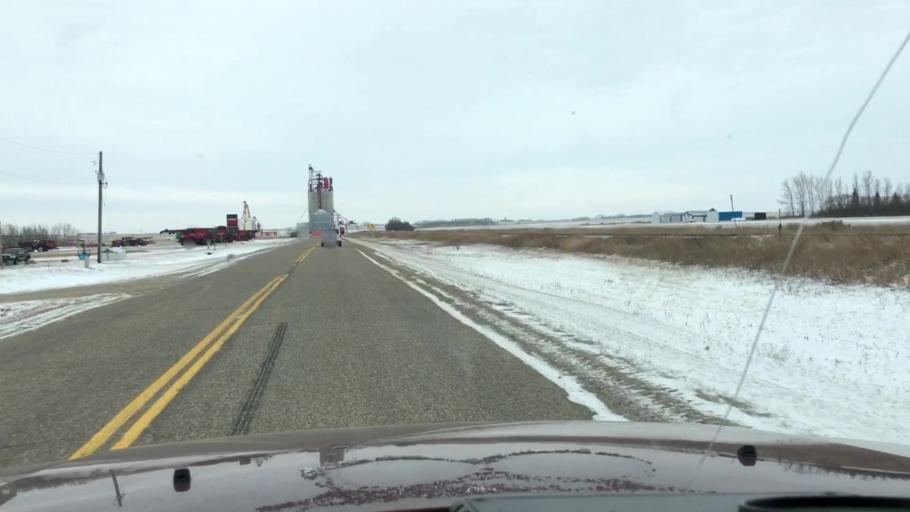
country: CA
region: Saskatchewan
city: Watrous
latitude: 51.2522
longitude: -105.9802
